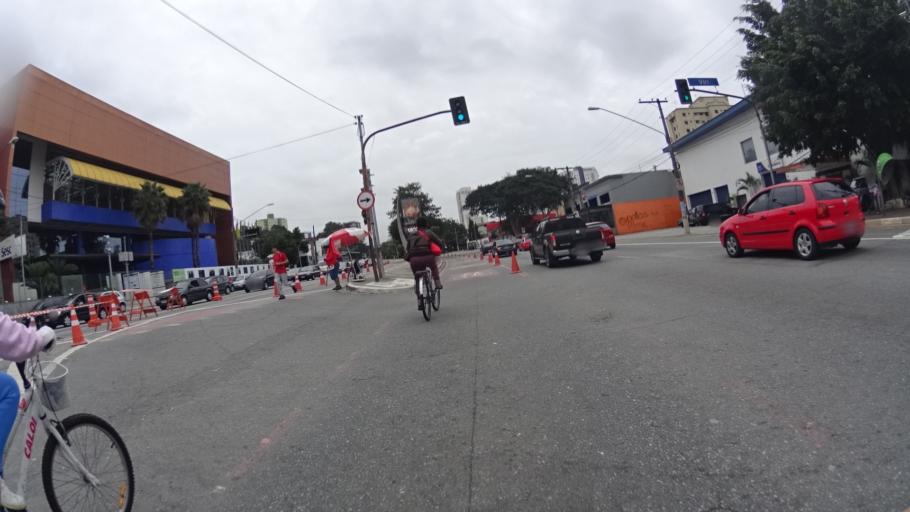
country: BR
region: Sao Paulo
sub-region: Sao Paulo
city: Sao Paulo
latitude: -23.4972
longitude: -46.6123
